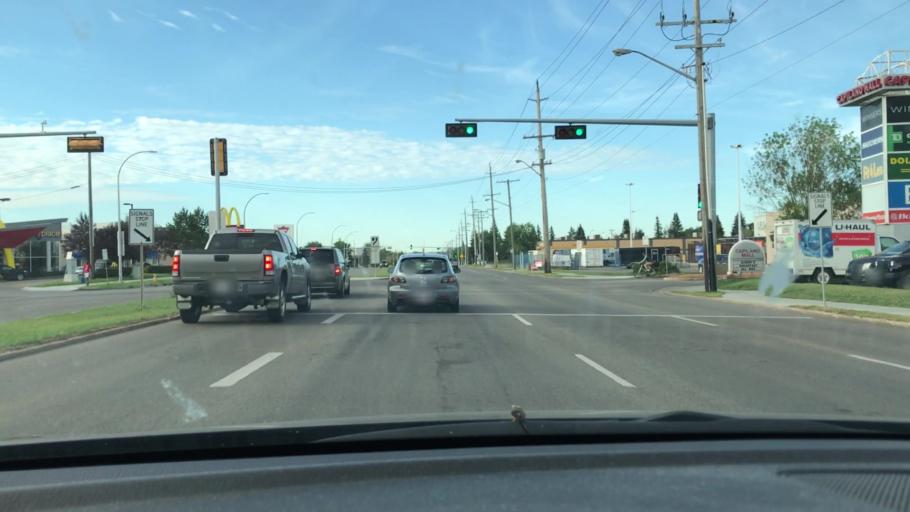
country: CA
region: Alberta
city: Edmonton
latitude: 53.5401
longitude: -113.4186
